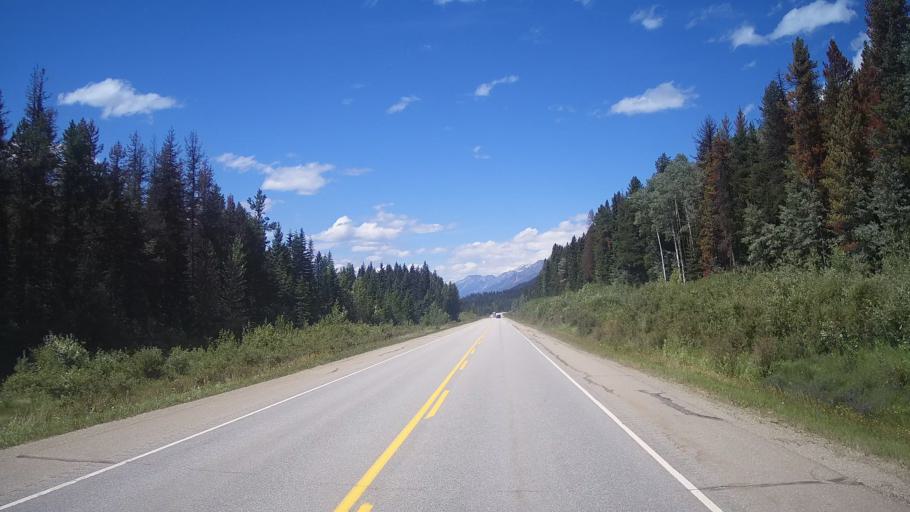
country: CA
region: Alberta
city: Jasper Park Lodge
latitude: 52.8813
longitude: -118.7084
